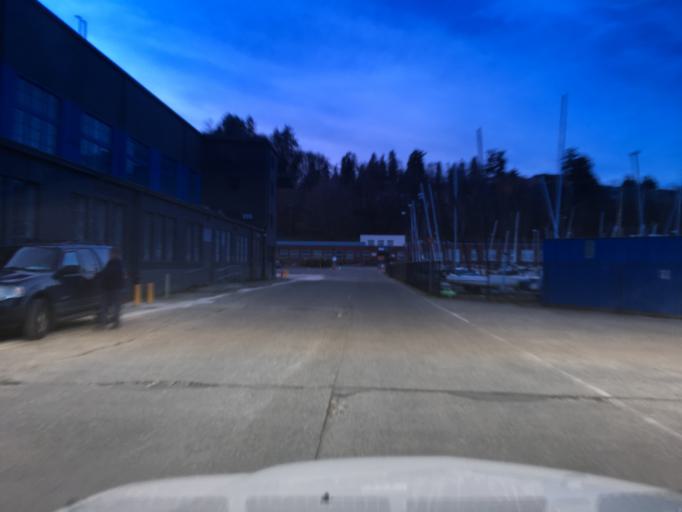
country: US
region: Washington
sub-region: King County
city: Inglewood-Finn Hill
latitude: 47.6876
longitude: -122.2629
